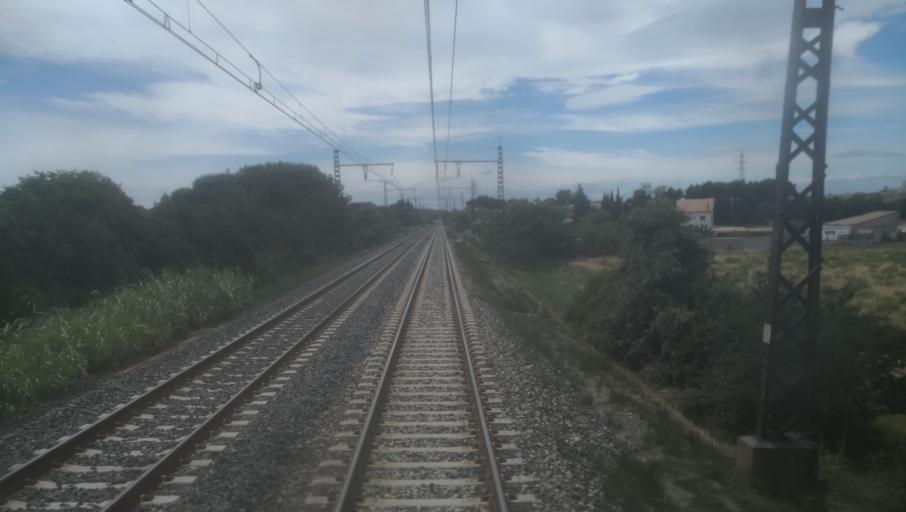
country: FR
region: Languedoc-Roussillon
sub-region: Departement de l'Herault
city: Villeneuve-les-Beziers
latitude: 43.3252
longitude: 3.2780
